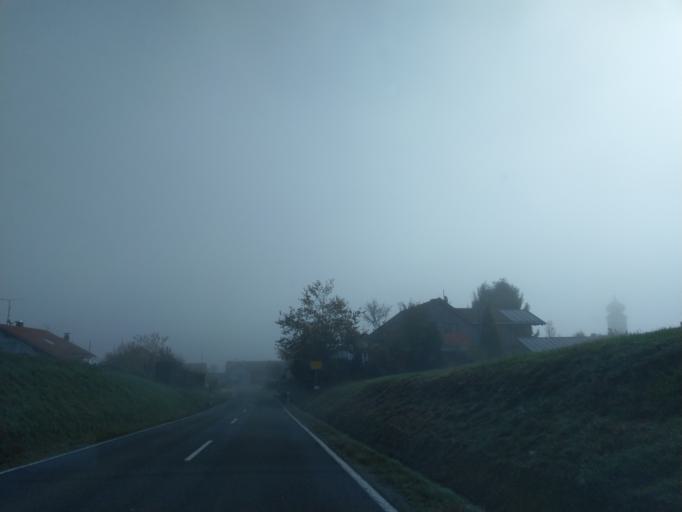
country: DE
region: Bavaria
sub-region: Lower Bavaria
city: Aussernzell
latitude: 48.7251
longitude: 13.2012
